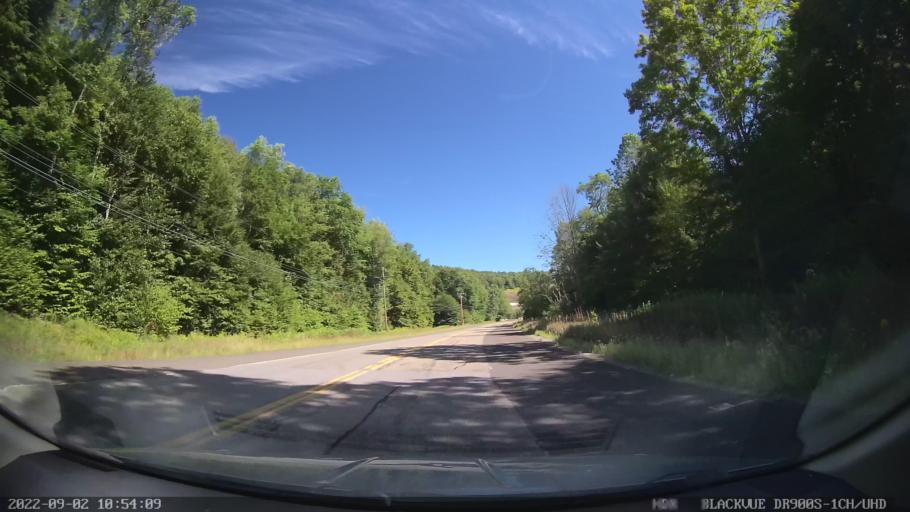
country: US
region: Pennsylvania
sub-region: Tioga County
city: Blossburg
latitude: 41.6558
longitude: -77.0943
